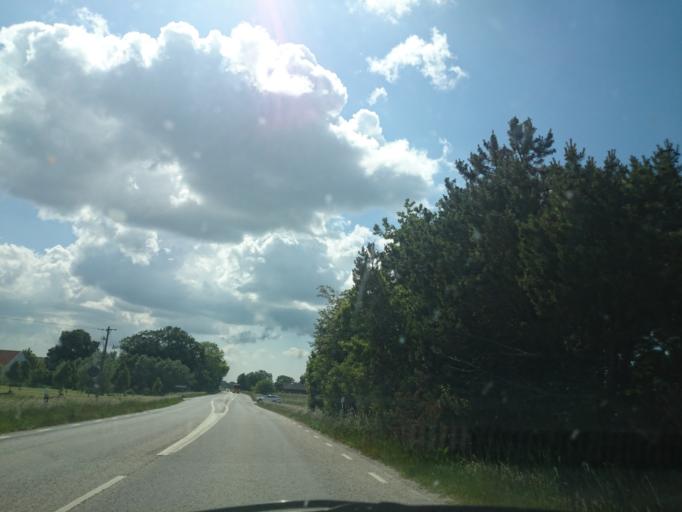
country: SE
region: Skane
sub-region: Lunds Kommun
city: Lund
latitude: 55.7115
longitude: 13.2768
